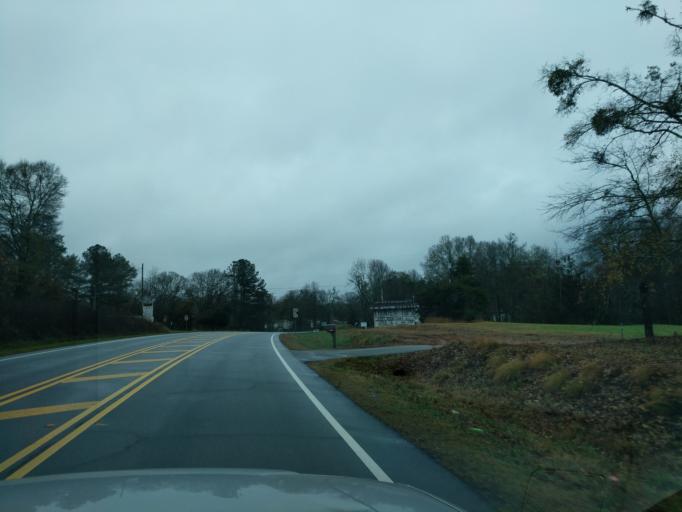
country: US
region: Georgia
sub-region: Franklin County
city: Lavonia
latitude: 34.3755
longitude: -83.0854
